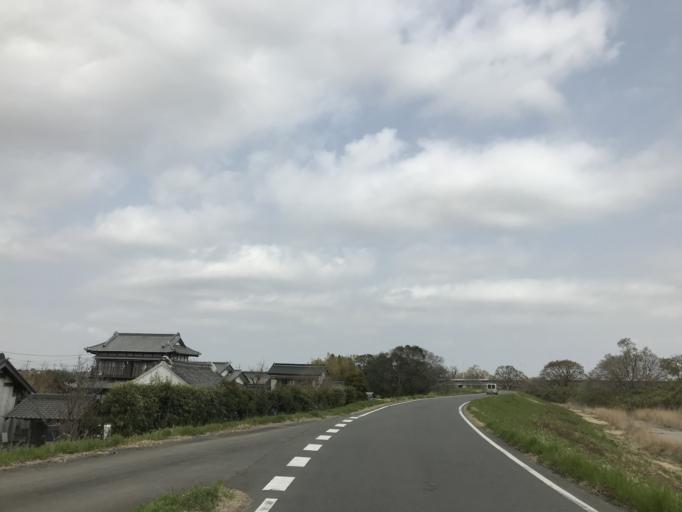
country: JP
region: Ibaraki
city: Mitsukaido
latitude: 36.0363
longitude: 140.0267
